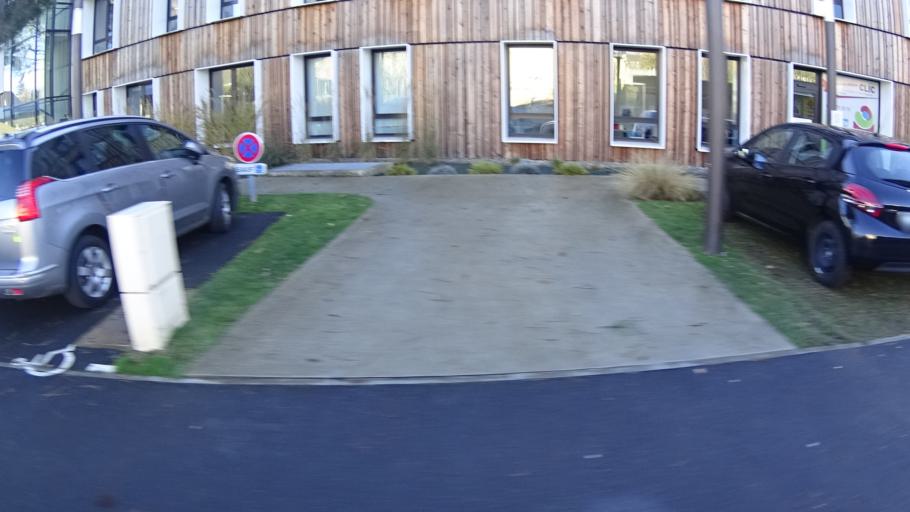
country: FR
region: Brittany
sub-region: Departement d'Ille-et-Vilaine
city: Redon
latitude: 47.6530
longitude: -2.0935
